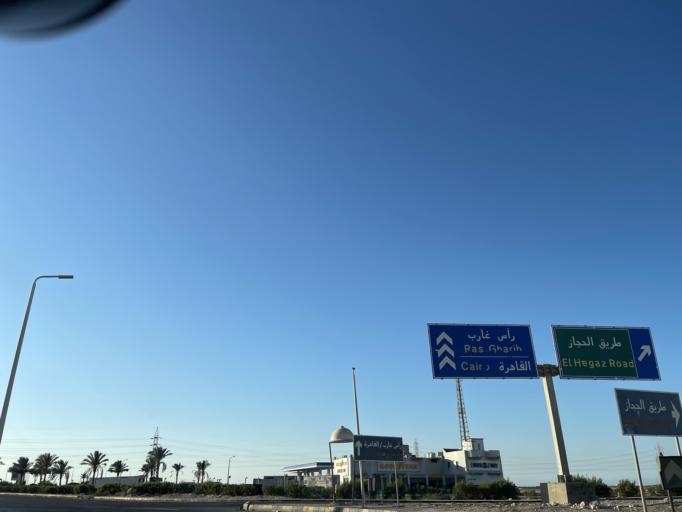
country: EG
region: Red Sea
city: Hurghada
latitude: 27.2317
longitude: 33.7818
